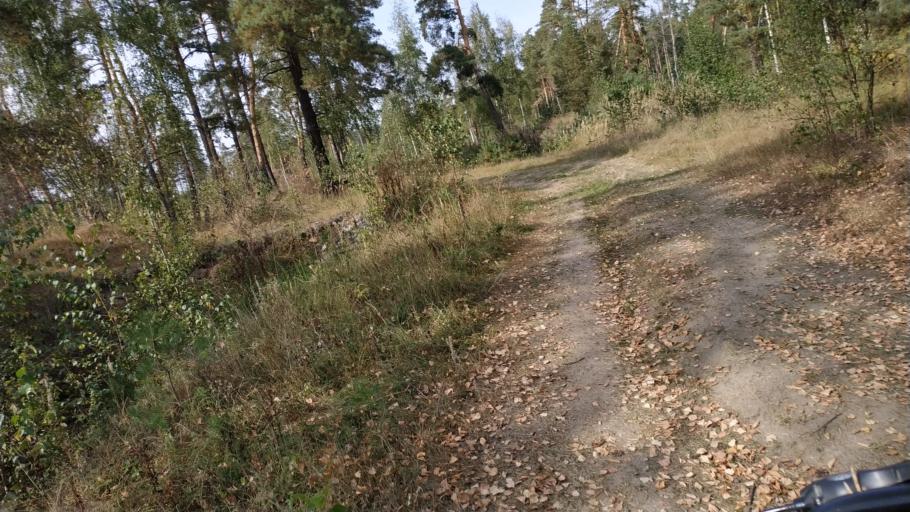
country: RU
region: Moskovskaya
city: Malyshevo
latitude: 55.5321
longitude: 38.2935
